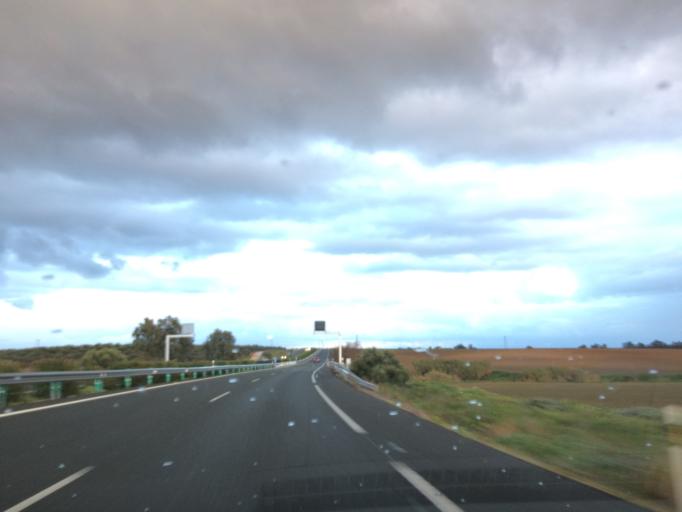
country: ES
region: Andalusia
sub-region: Provincia de Sevilla
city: Mairena del Alcor
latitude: 37.3215
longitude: -5.7696
